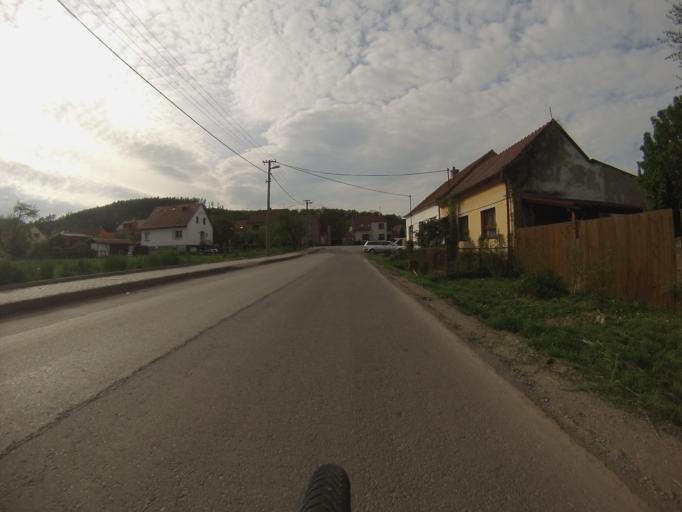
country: CZ
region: South Moravian
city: Cebin
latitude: 49.3136
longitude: 16.4527
